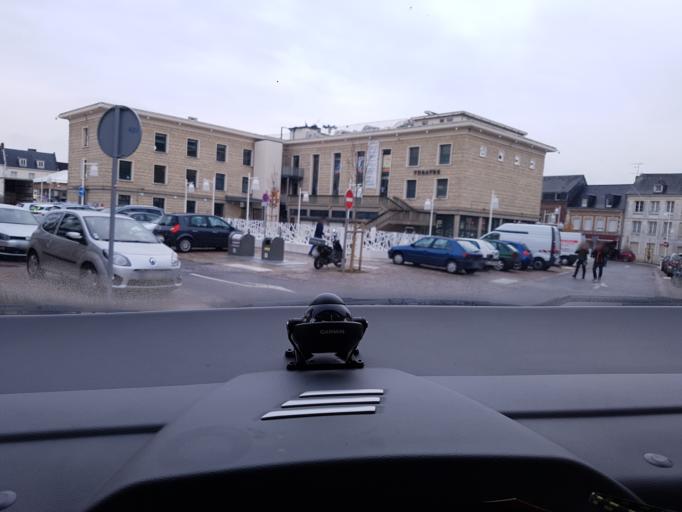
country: FR
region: Haute-Normandie
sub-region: Departement de la Seine-Maritime
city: Duclair
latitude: 49.4834
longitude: 0.8756
